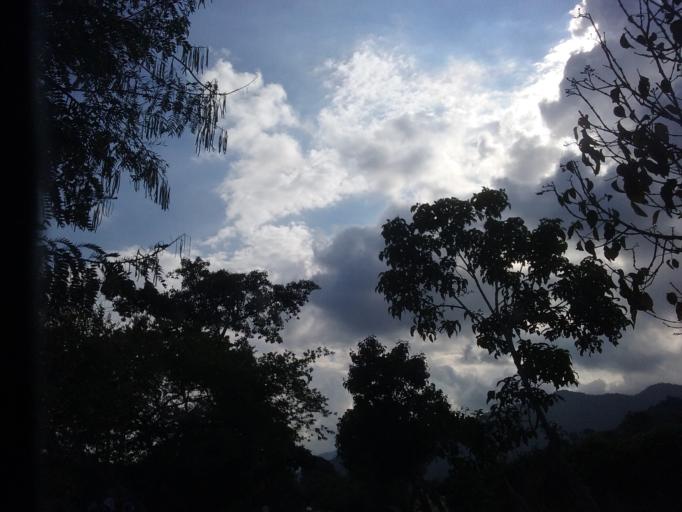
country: CO
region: Tolima
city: Libano
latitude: 4.8926
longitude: -75.0339
